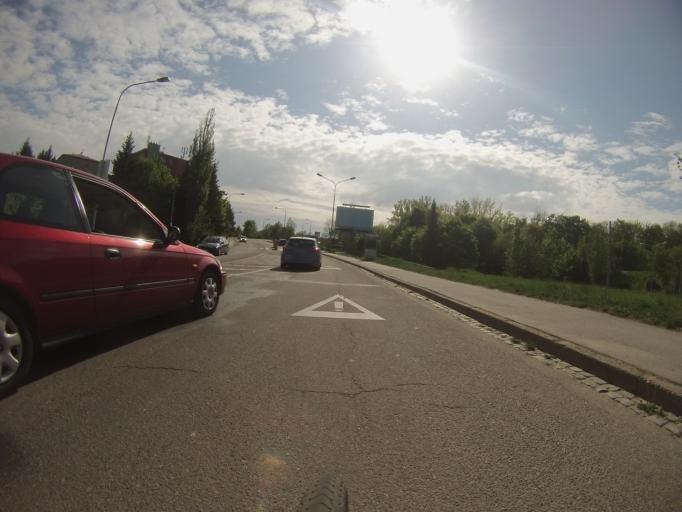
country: CZ
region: South Moravian
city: Troubsko
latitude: 49.2280
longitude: 16.5222
